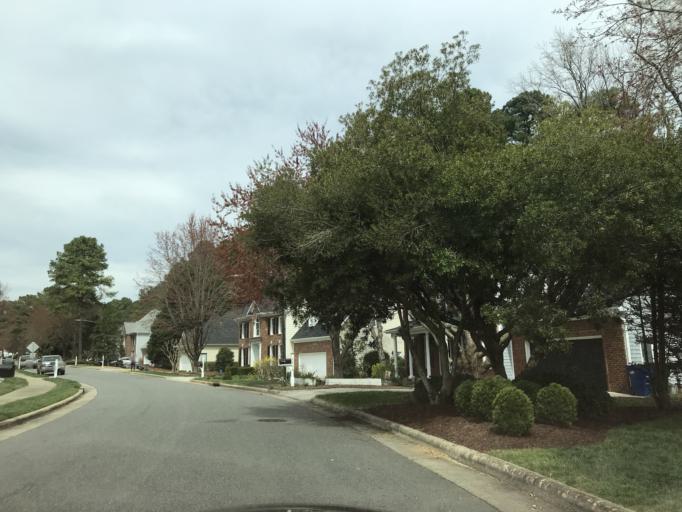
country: US
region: North Carolina
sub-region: Wake County
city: West Raleigh
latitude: 35.8844
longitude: -78.6852
